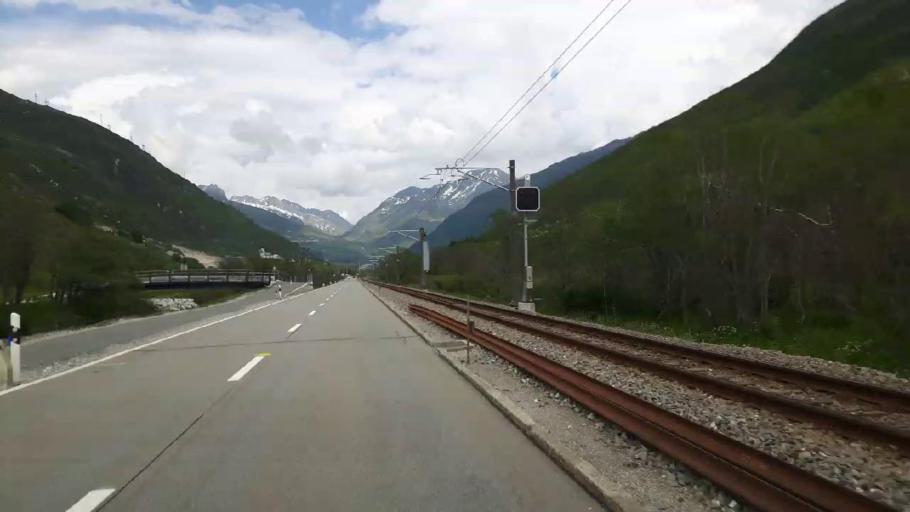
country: CH
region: Uri
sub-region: Uri
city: Andermatt
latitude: 46.6077
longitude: 8.5286
